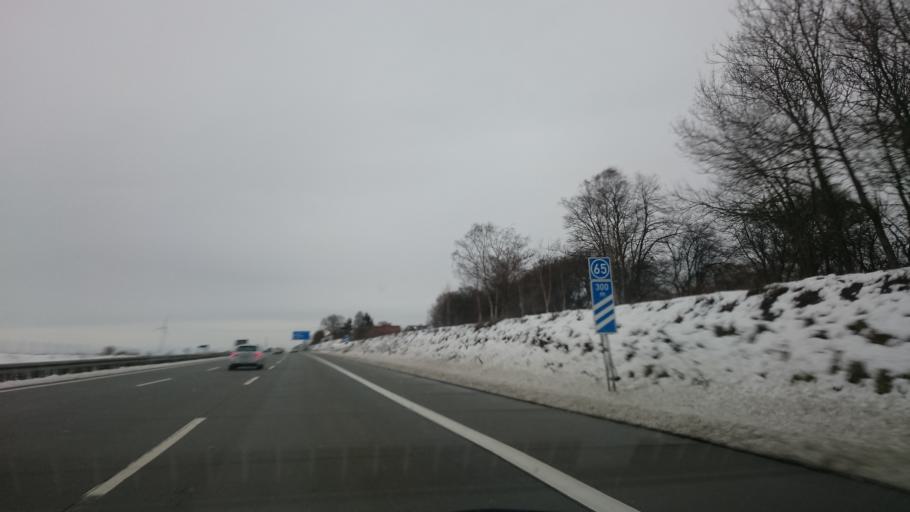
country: DE
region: Saxony
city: Callenberg
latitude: 50.8178
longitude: 12.6529
